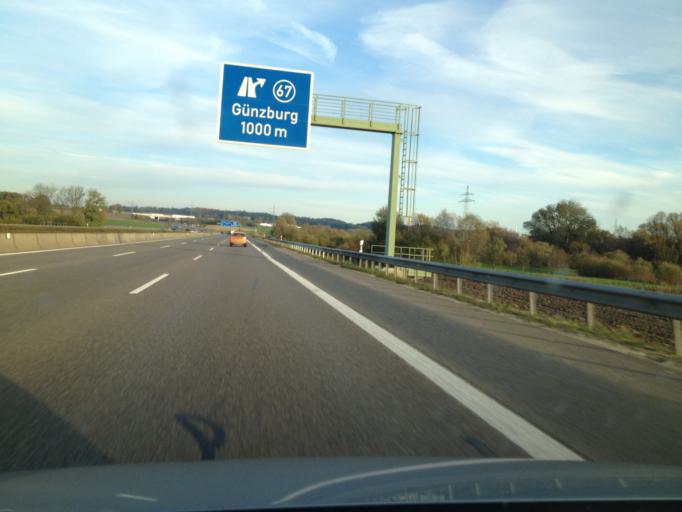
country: DE
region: Bavaria
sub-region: Swabia
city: Wasserburg
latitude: 48.4300
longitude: 10.2768
